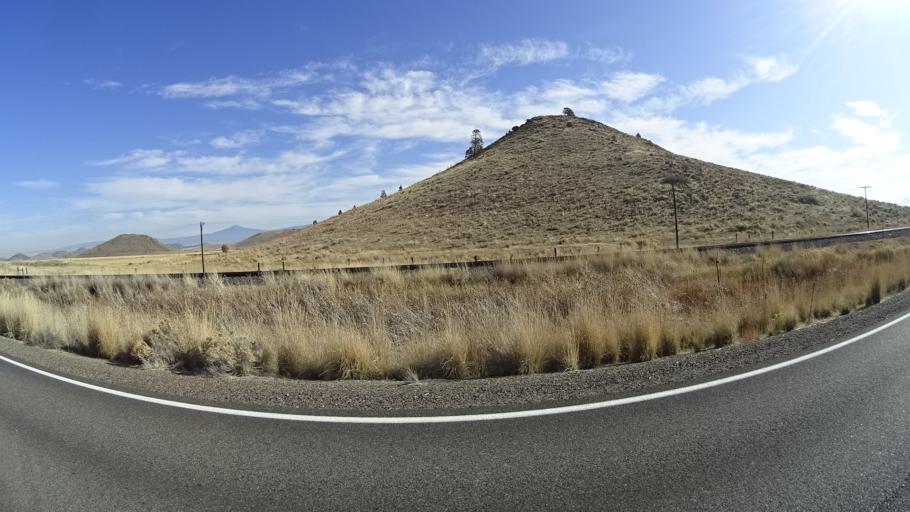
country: US
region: California
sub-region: Siskiyou County
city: Weed
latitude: 41.5348
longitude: -122.5247
